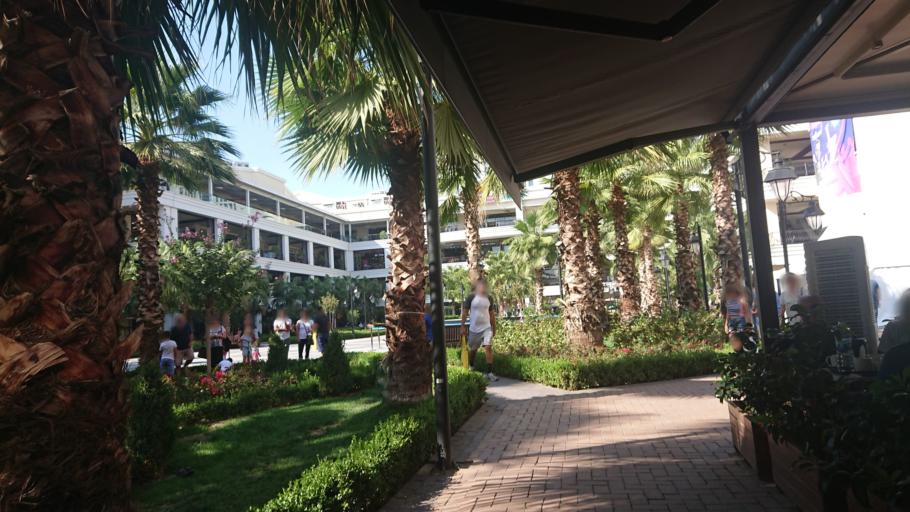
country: TR
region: Izmir
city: Karsiyaka
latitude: 38.4734
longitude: 27.0747
